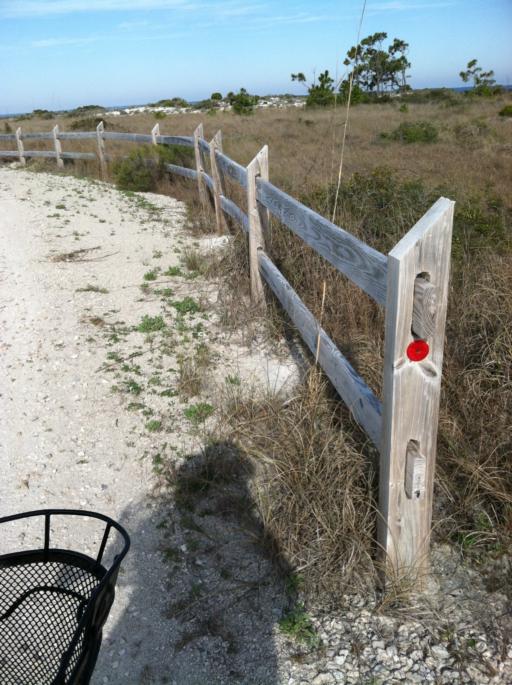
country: US
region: Florida
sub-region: Franklin County
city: Eastpoint
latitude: 29.7274
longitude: -84.7353
